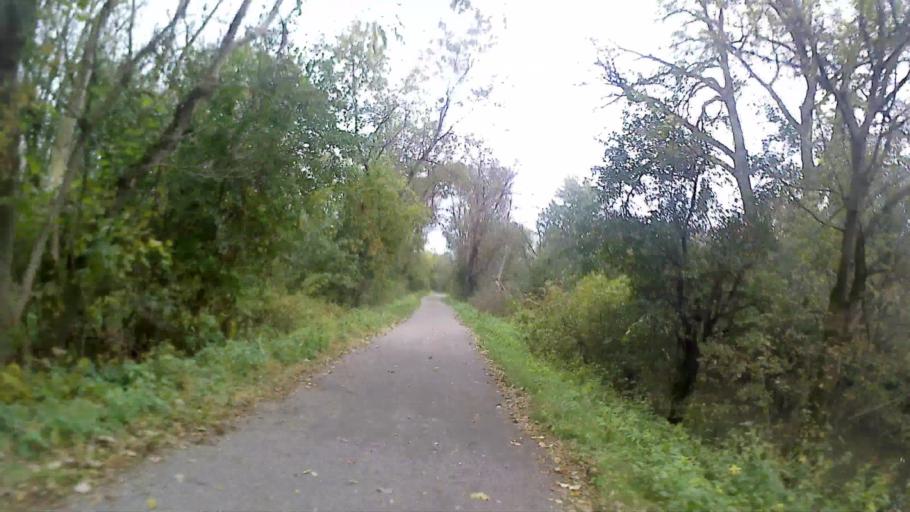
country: US
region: Illinois
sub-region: Kane County
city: Sugar Grove
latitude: 41.7757
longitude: -88.4171
